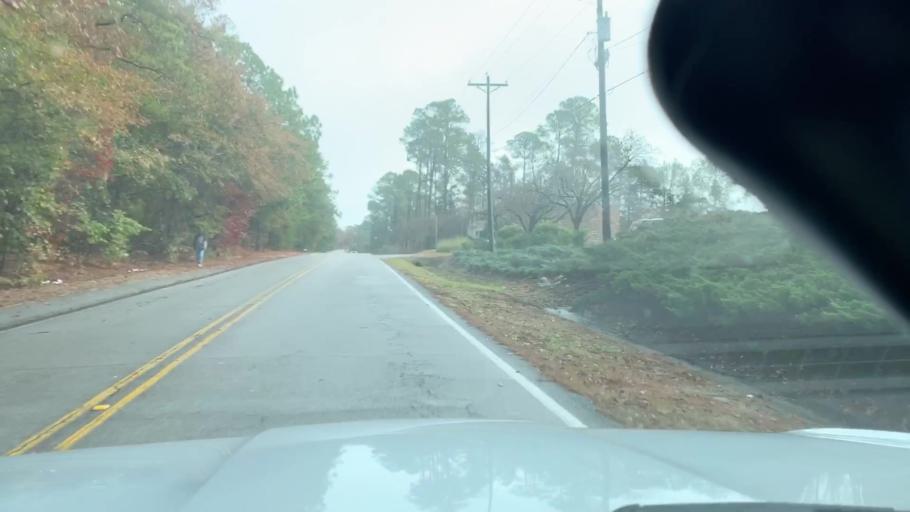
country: US
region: South Carolina
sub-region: Richland County
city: Woodfield
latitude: 34.0619
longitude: -80.9426
